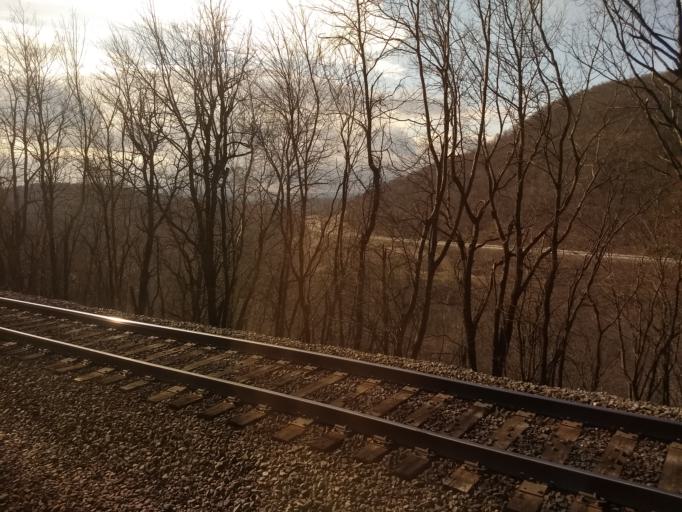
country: US
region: Pennsylvania
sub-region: Cambria County
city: Gallitzin
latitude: 40.4748
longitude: -78.4880
